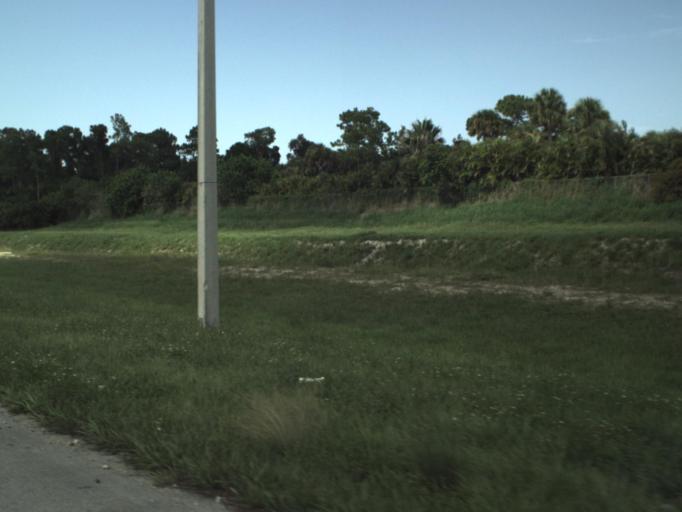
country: US
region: Florida
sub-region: Palm Beach County
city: Royal Palm Beach
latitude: 26.7031
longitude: -80.2010
